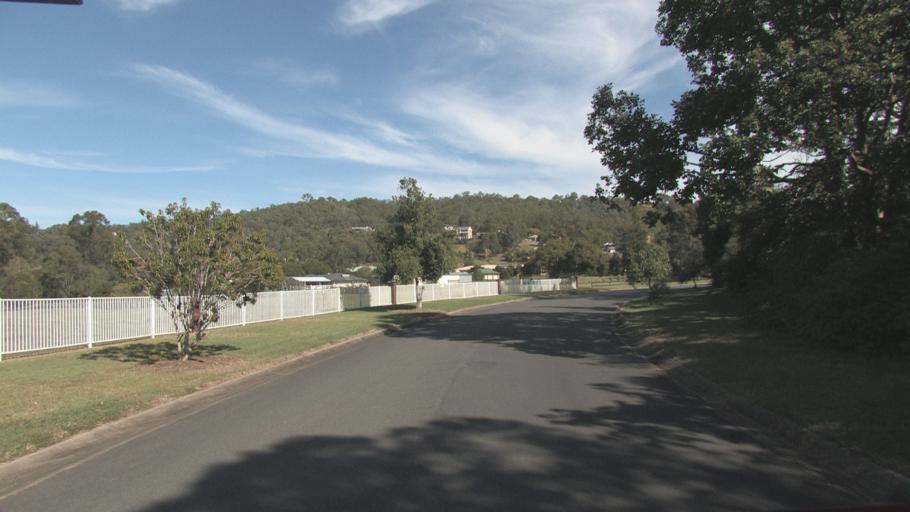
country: AU
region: Queensland
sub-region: Logan
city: Windaroo
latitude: -27.7576
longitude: 153.1824
